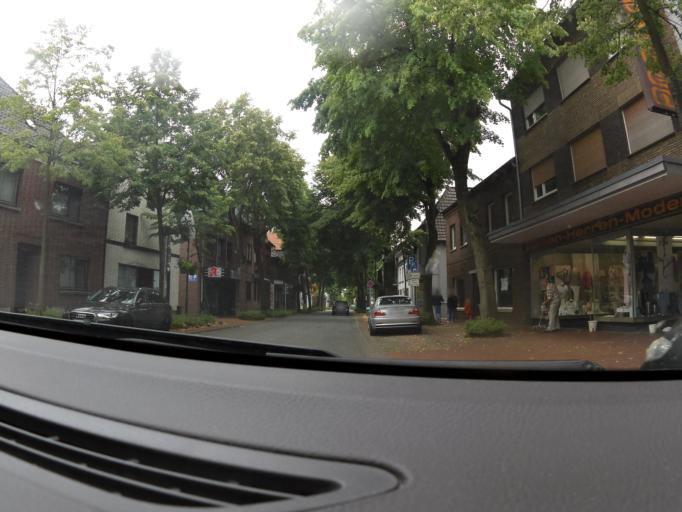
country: DE
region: North Rhine-Westphalia
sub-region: Regierungsbezirk Dusseldorf
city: Sonsbeck
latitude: 51.6084
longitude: 6.3762
